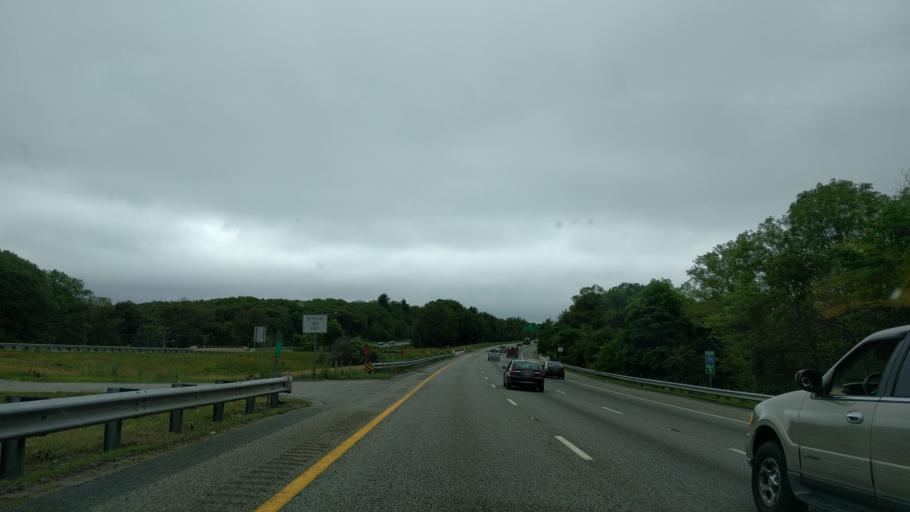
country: US
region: Rhode Island
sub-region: Providence County
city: Johnston
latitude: 41.8129
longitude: -71.5098
